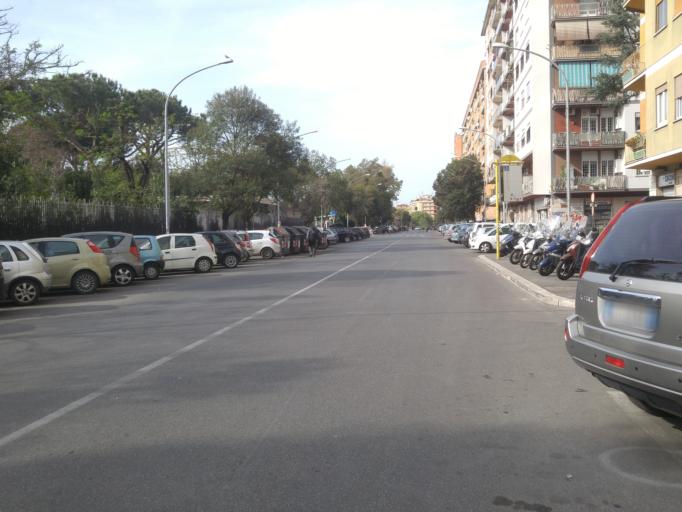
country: IT
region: Latium
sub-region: Citta metropolitana di Roma Capitale
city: Rome
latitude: 41.8649
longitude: 12.4845
